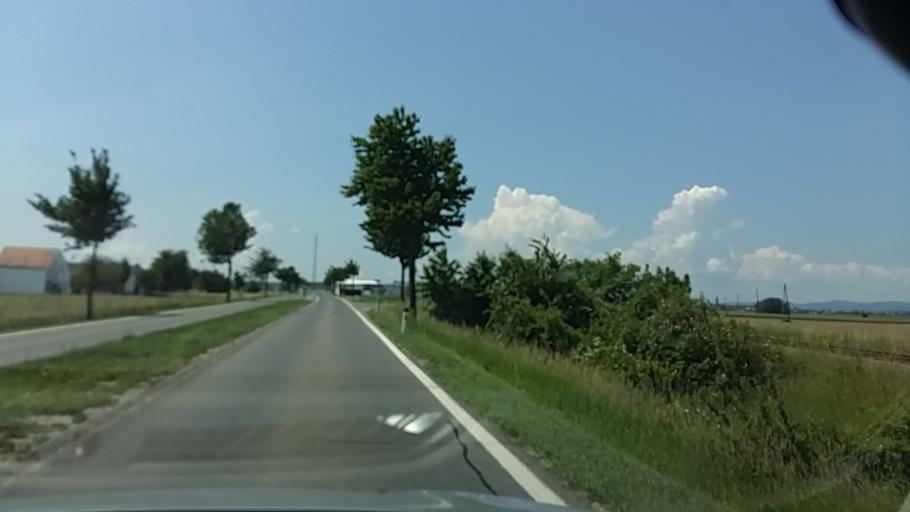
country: AT
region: Burgenland
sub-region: Politischer Bezirk Oberpullendorf
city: Deutschkreutz
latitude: 47.6009
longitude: 16.6030
